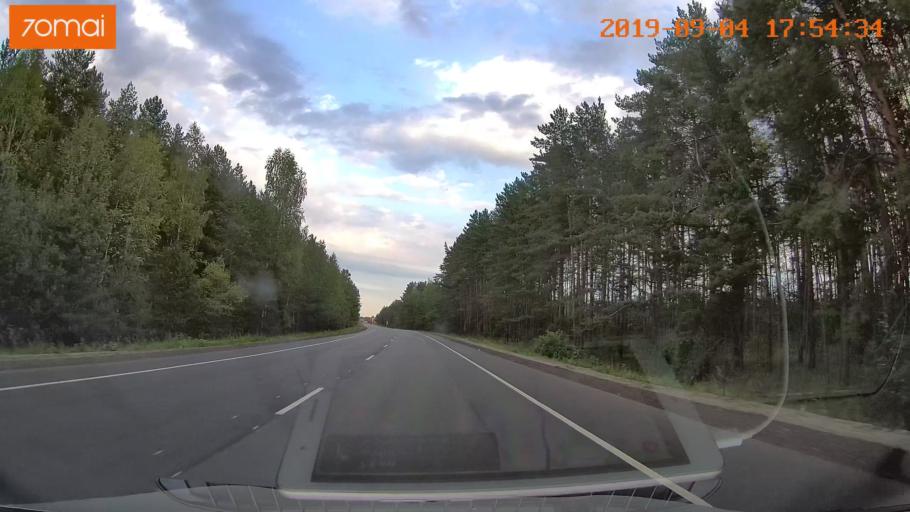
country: RU
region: Moskovskaya
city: Imeni Tsyurupy
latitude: 55.5097
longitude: 38.7480
